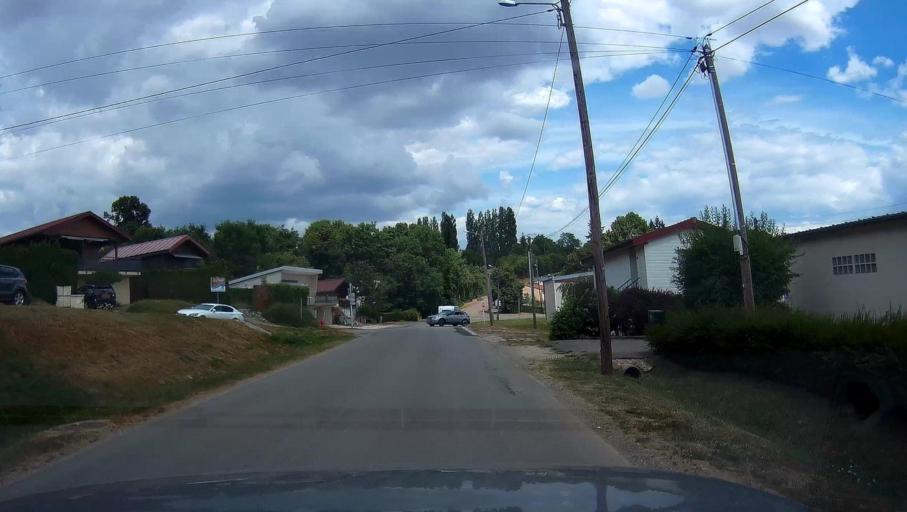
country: FR
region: Champagne-Ardenne
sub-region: Departement de la Haute-Marne
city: Langres
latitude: 47.8691
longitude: 5.3728
